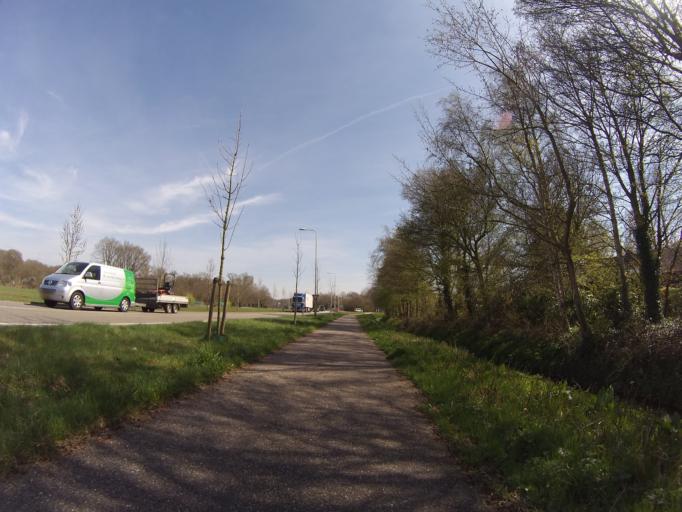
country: NL
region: Gelderland
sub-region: Gemeente Nijkerk
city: Nijkerk
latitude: 52.2325
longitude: 5.4909
